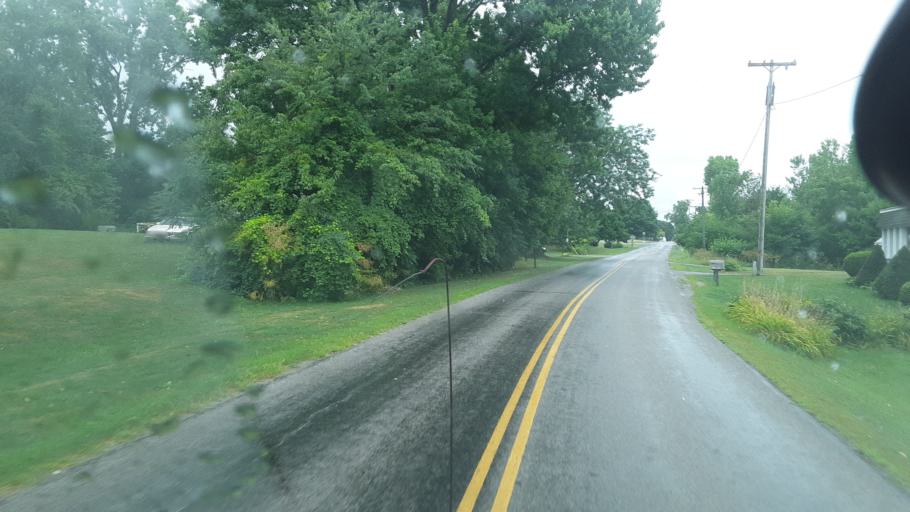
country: US
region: Indiana
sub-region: Steuben County
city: Hamilton
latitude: 41.6350
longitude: -84.7890
